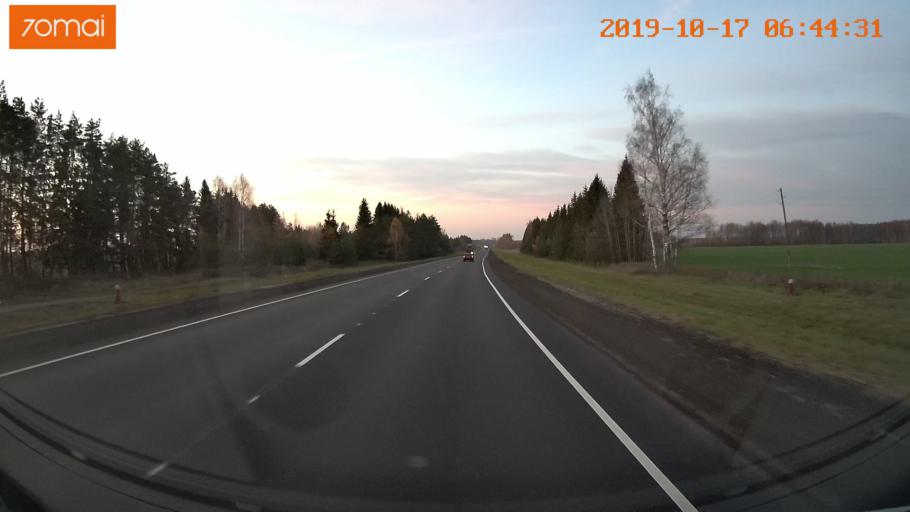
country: RU
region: Vladimir
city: Kideksha
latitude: 56.5713
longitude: 40.5539
